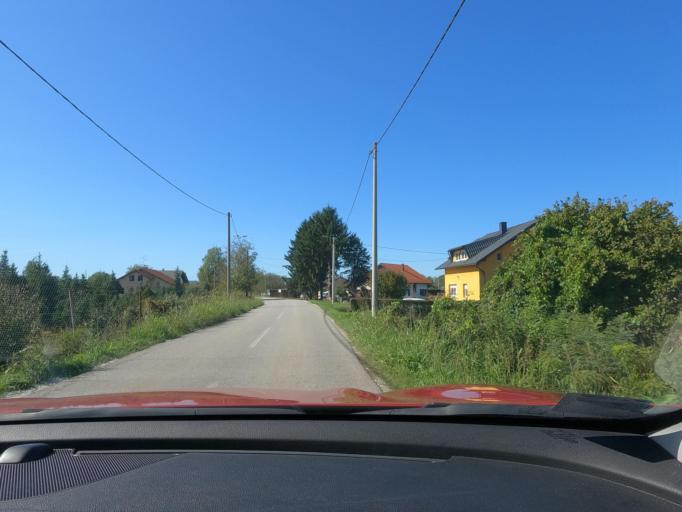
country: HR
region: Sisacko-Moslavacka
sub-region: Grad Sisak
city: Sisak
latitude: 45.4923
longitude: 16.3420
